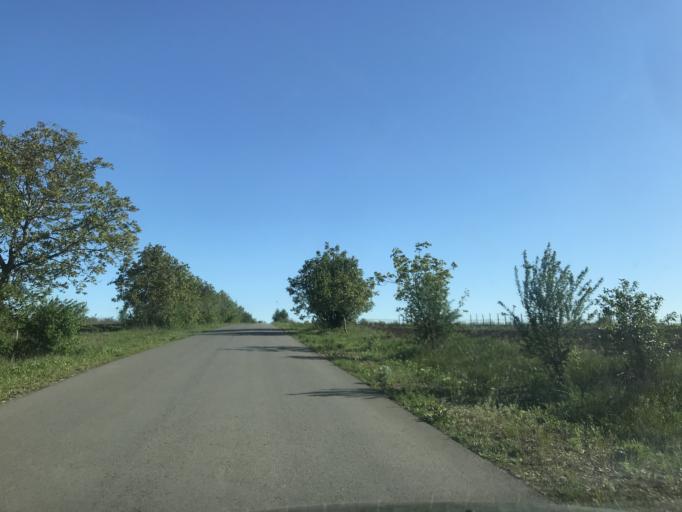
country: MD
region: Chisinau
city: Cricova
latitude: 47.2430
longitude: 28.8160
